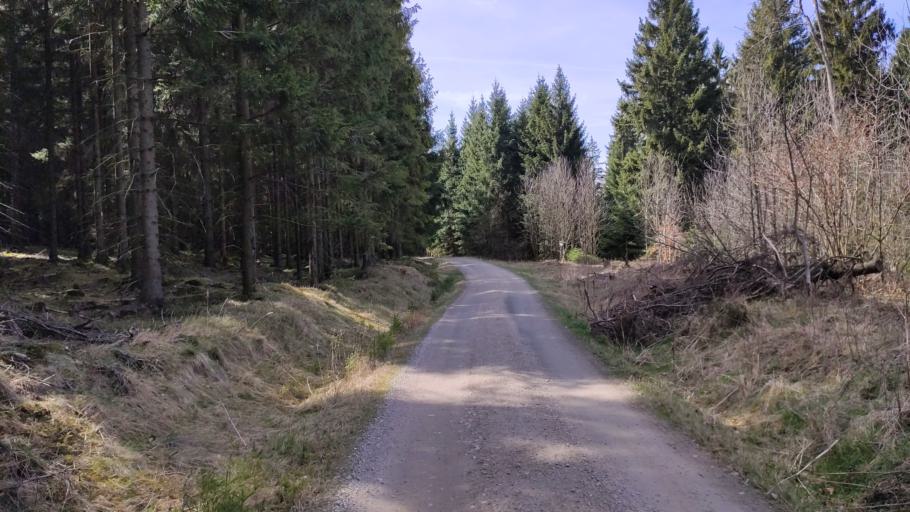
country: DE
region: Bavaria
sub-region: Upper Franconia
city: Reichenbach
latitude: 50.4626
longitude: 11.4536
